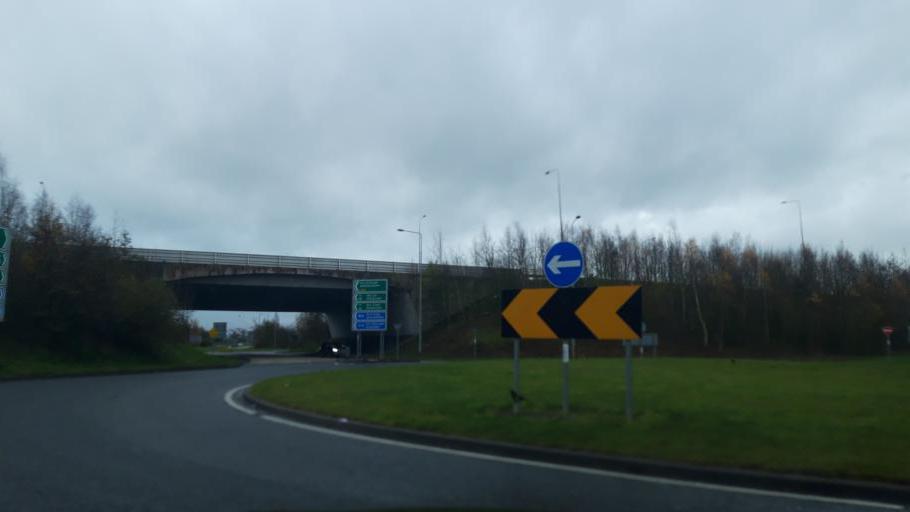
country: IE
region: Leinster
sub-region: County Carlow
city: Carlow
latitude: 52.8021
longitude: -6.8819
